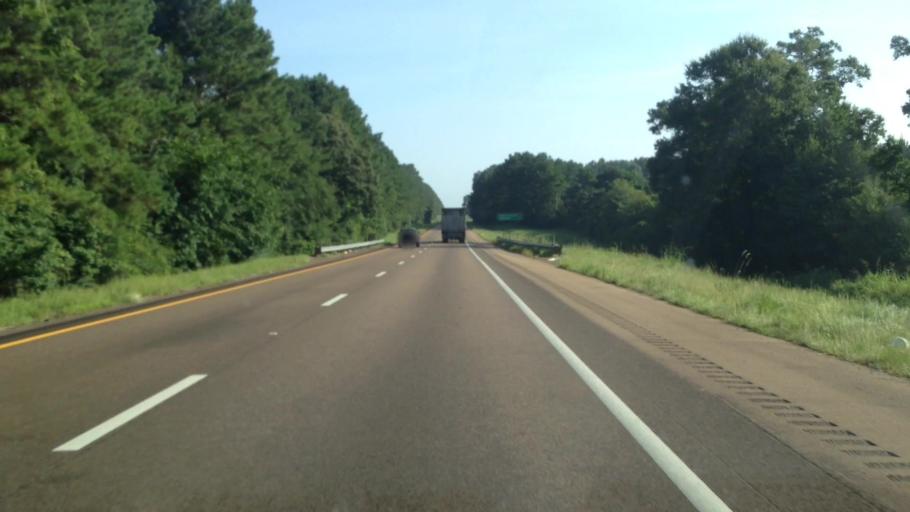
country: US
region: Mississippi
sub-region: Pike County
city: Summit
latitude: 31.3008
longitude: -90.4780
